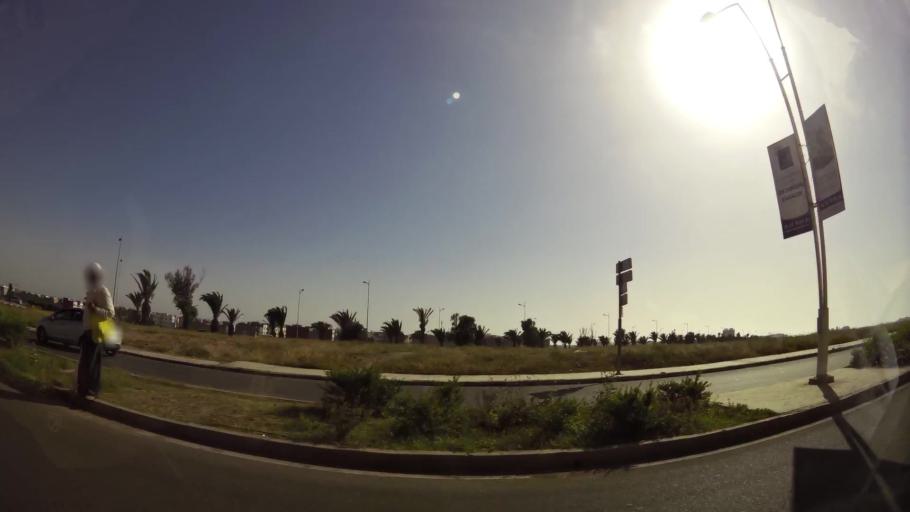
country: MA
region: Oued ed Dahab-Lagouira
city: Dakhla
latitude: 30.4044
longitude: -9.5605
